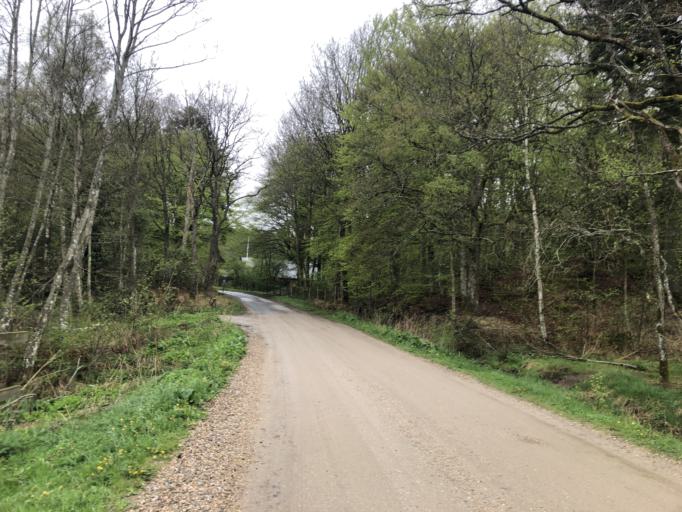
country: DK
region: Central Jutland
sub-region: Lemvig Kommune
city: Lemvig
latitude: 56.4853
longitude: 8.3613
